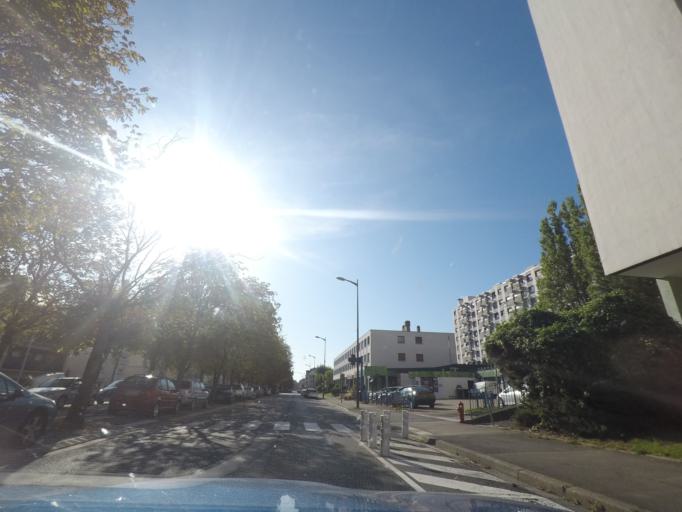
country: FR
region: Lorraine
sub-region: Departement de la Moselle
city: Thionville
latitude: 49.3620
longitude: 6.1563
